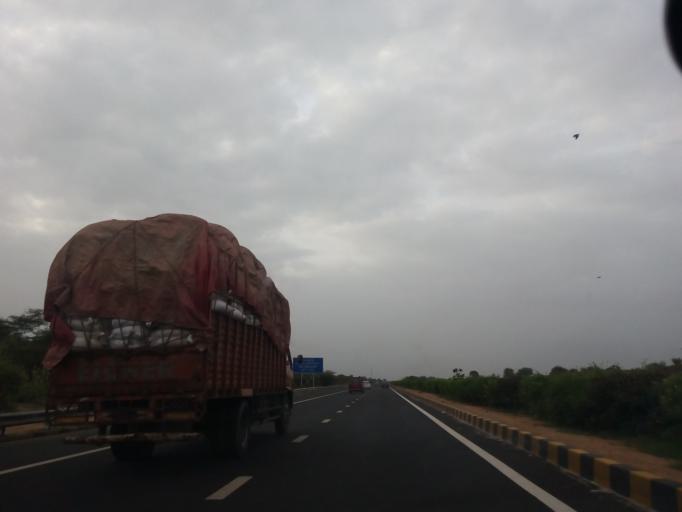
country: IN
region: Gujarat
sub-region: Kheda
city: Mahemdavad
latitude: 22.9061
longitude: 72.7702
